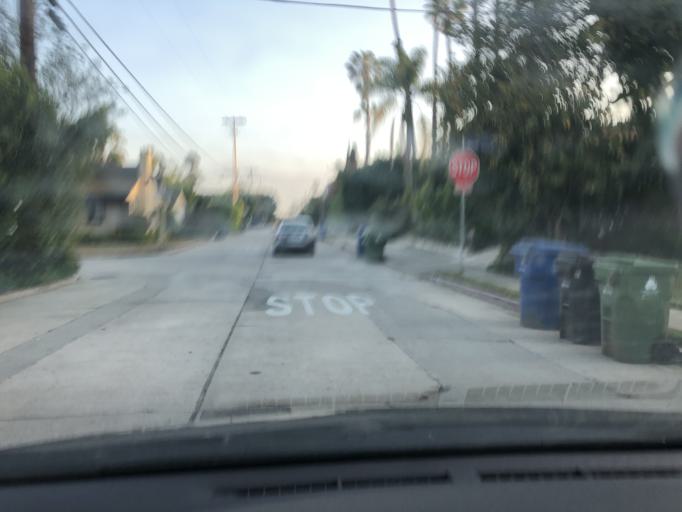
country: US
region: California
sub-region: Los Angeles County
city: Culver City
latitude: 34.0341
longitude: -118.4006
